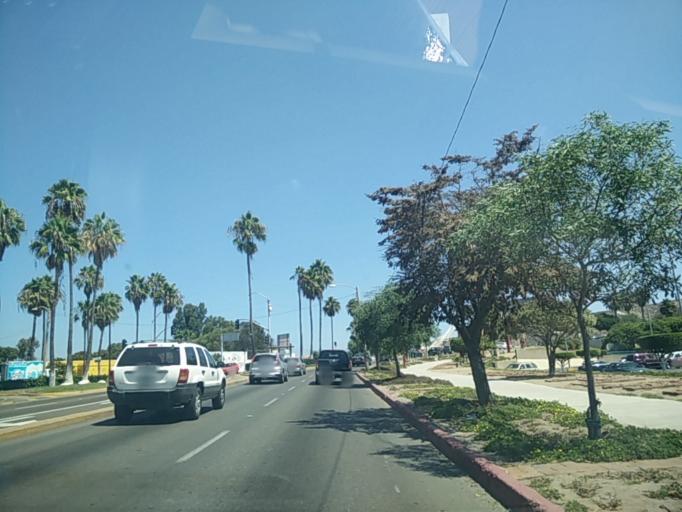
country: US
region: California
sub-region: San Diego County
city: Imperial Beach
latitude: 32.5330
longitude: -117.1139
